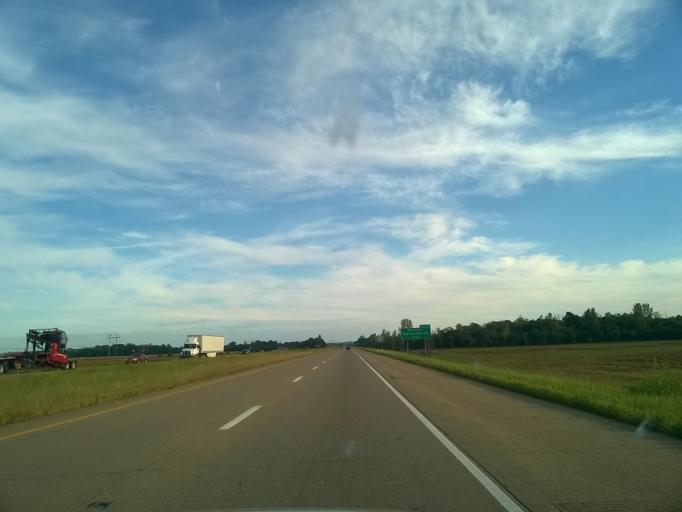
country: US
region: Indiana
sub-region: Vanderburgh County
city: Melody Hill
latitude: 38.0688
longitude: -87.4757
